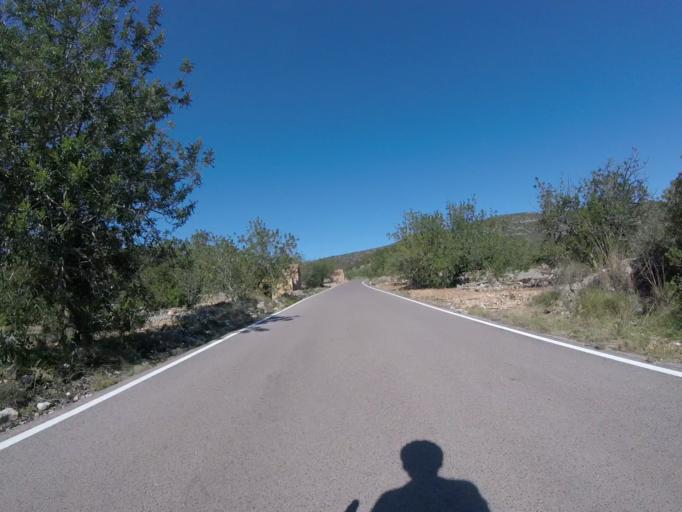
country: ES
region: Valencia
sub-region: Provincia de Castello
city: Santa Magdalena de Pulpis
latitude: 40.3817
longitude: 0.2632
